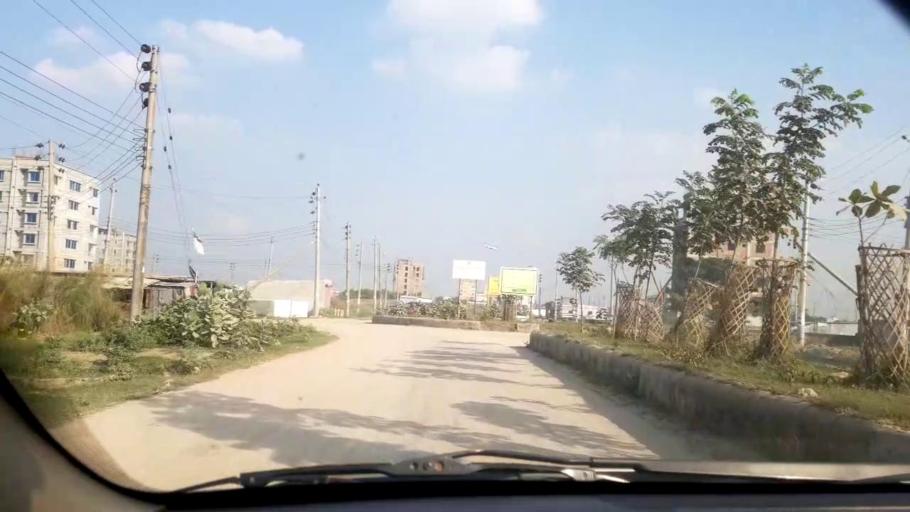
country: BD
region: Dhaka
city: Tungi
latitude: 23.8676
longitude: 90.3701
